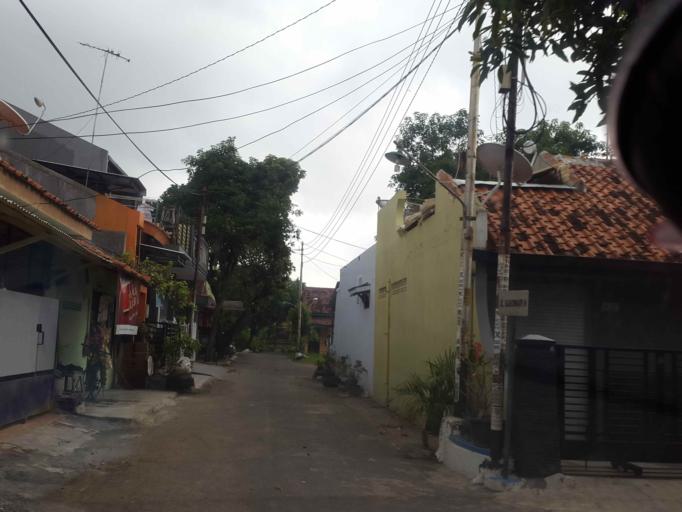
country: ID
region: Central Java
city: Tegal
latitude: -6.8758
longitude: 109.1429
